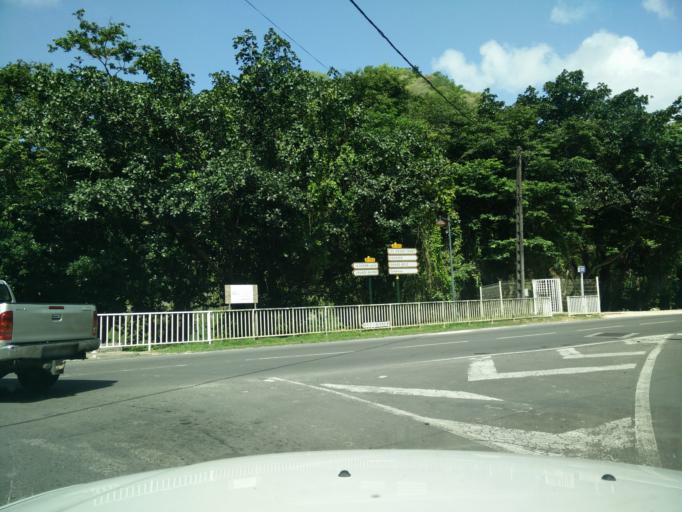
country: GP
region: Guadeloupe
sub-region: Guadeloupe
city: Le Gosier
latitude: 16.2183
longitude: -61.4774
